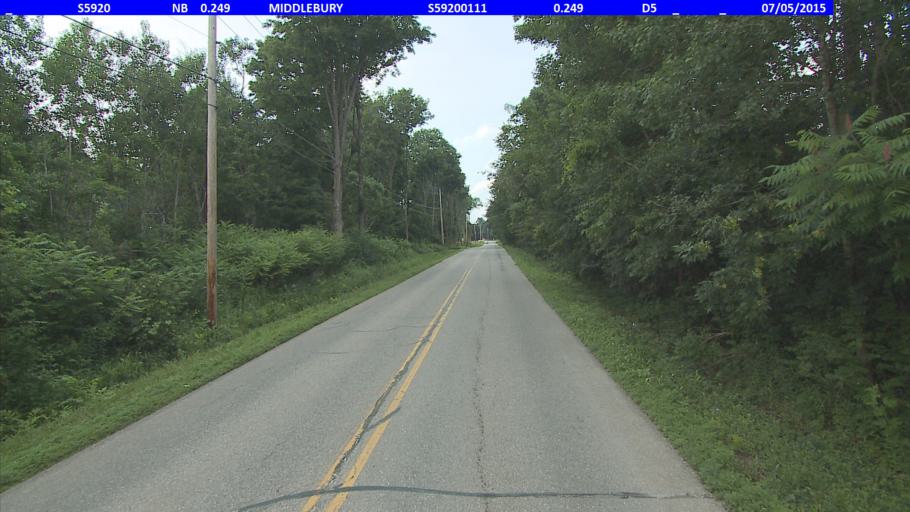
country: US
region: Vermont
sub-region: Addison County
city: Middlebury (village)
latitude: 43.9918
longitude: -73.1348
